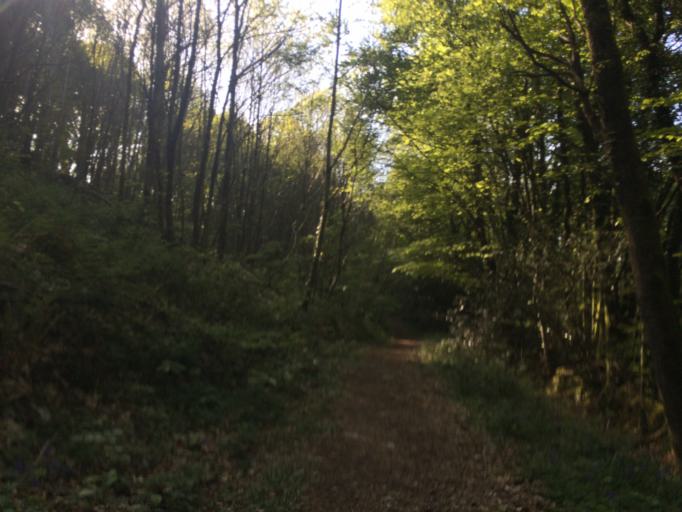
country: FR
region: Brittany
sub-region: Departement du Finistere
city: Daoulas
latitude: 48.3570
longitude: -4.2496
